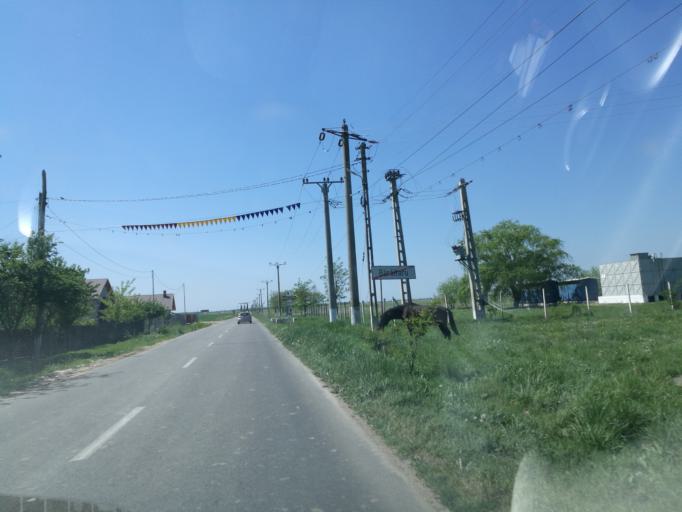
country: RO
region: Prahova
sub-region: Comuna Draganesti
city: Meri
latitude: 44.8579
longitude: 26.3446
